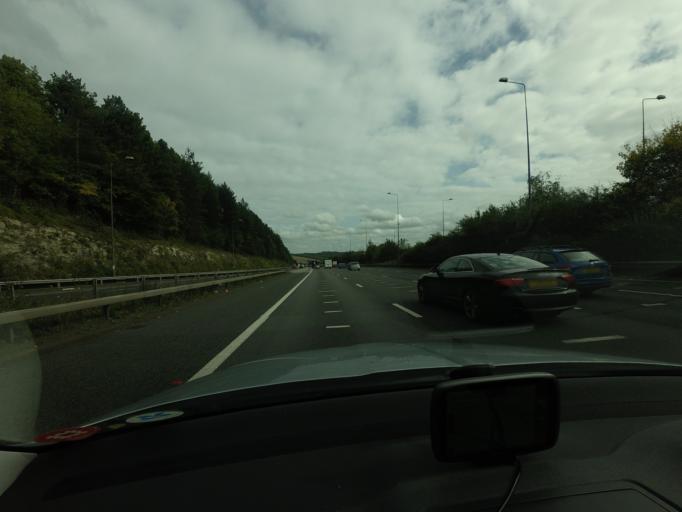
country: GB
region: England
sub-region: Surrey
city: Redhill
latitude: 51.2610
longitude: -0.1895
